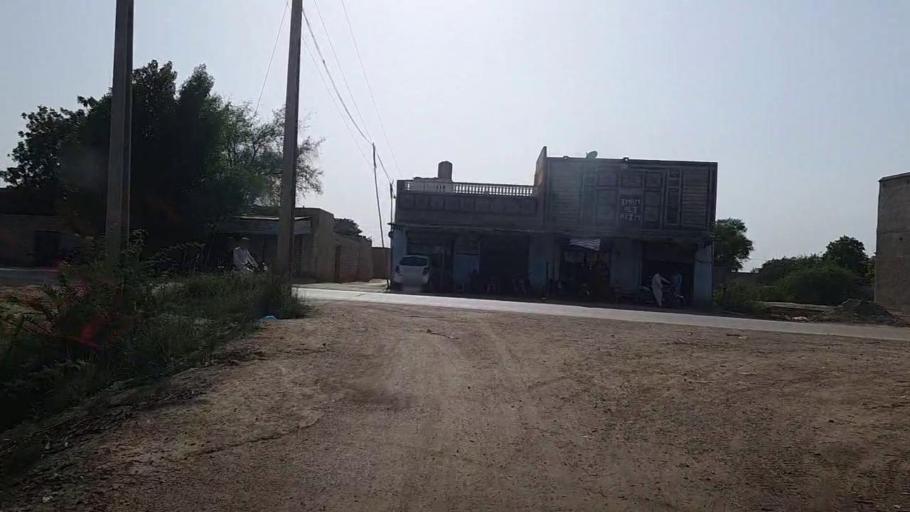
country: PK
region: Sindh
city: Karaundi
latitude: 26.8590
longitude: 68.3601
